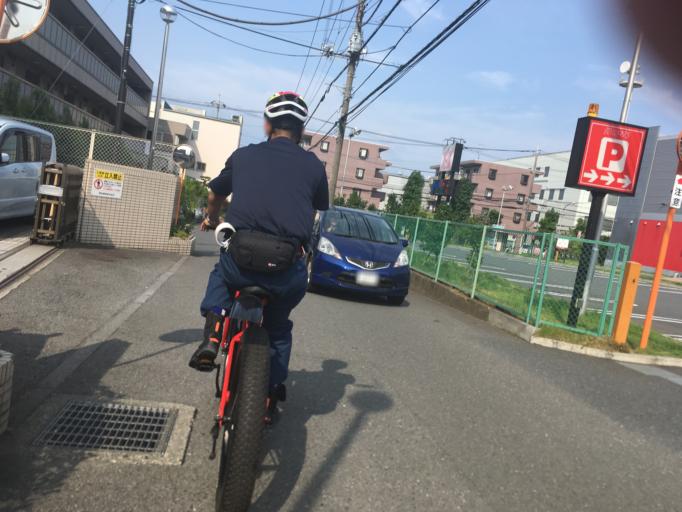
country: JP
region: Kanagawa
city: Minami-rinkan
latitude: 35.4769
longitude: 139.4623
